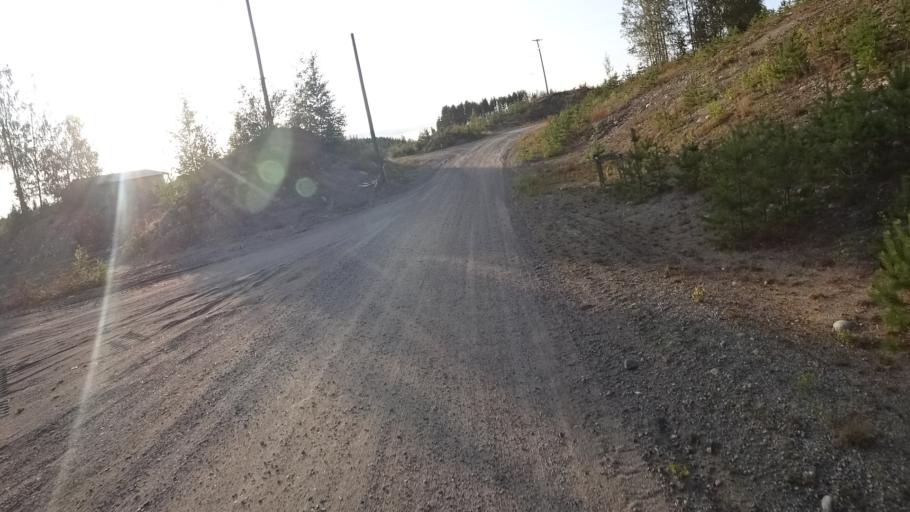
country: FI
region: North Karelia
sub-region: Joensuu
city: Ilomantsi
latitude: 62.6398
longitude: 31.0731
